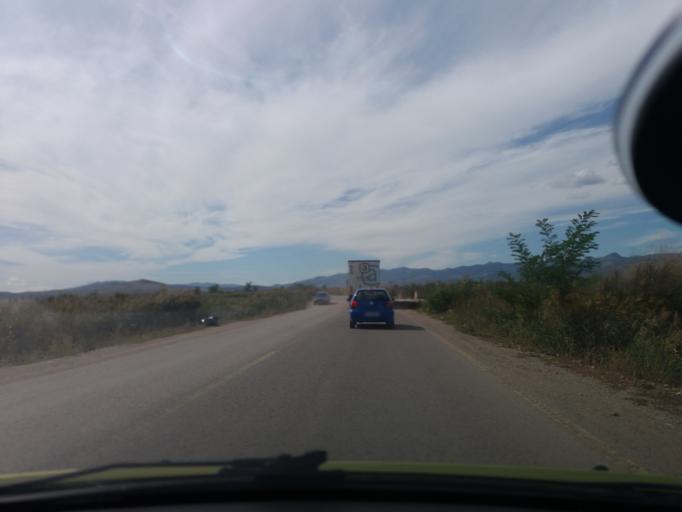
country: RO
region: Alba
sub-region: Oras Teius
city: Teius
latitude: 46.1698
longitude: 23.6924
